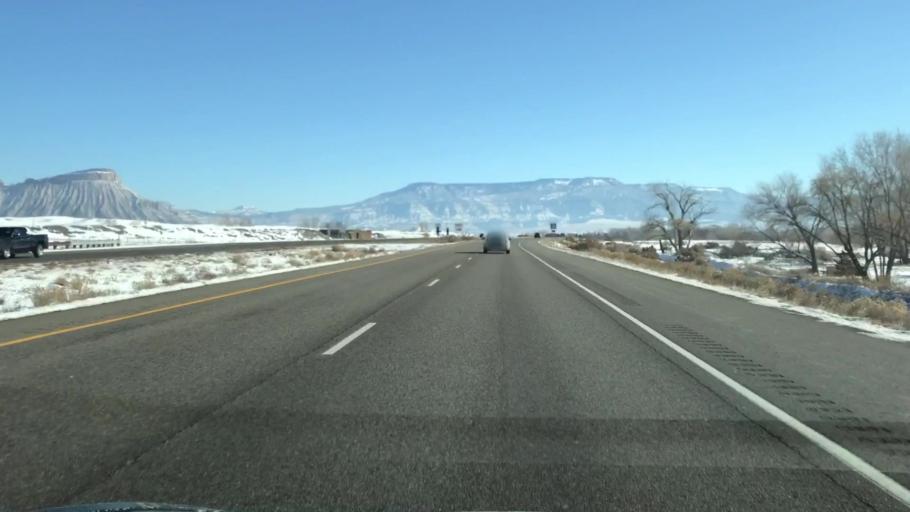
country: US
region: Colorado
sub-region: Mesa County
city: Fruitvale
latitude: 39.1077
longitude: -108.4976
